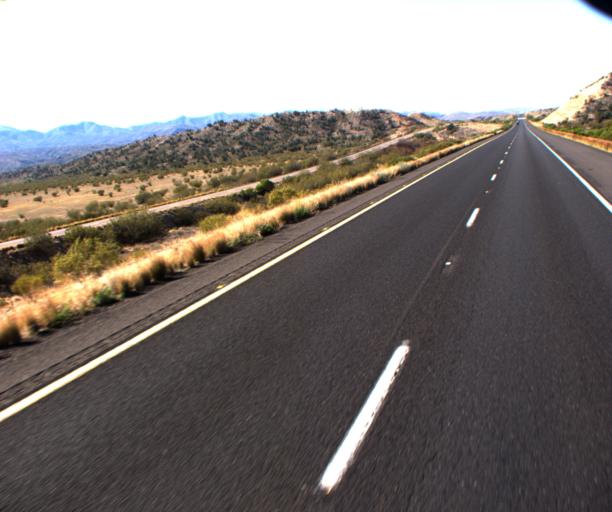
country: US
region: Arizona
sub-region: Mohave County
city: Kingman
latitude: 35.0869
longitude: -113.6662
